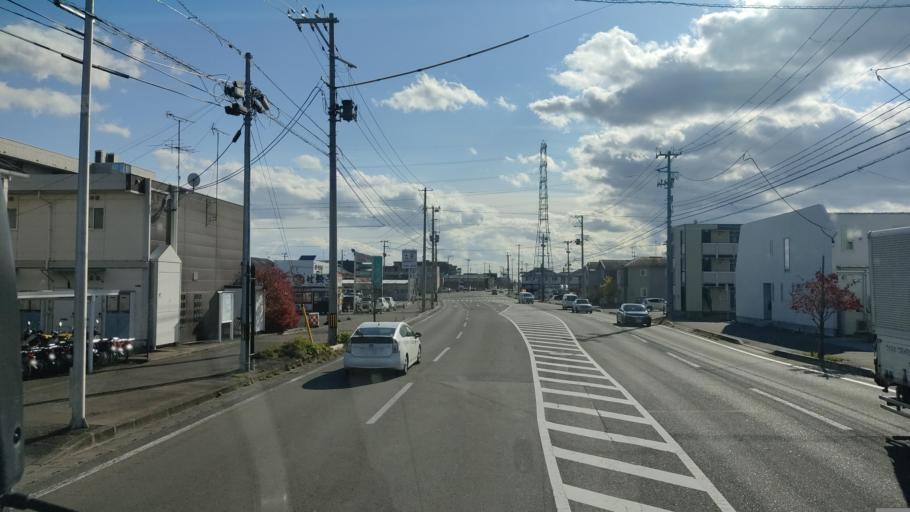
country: JP
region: Iwate
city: Morioka-shi
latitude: 39.6811
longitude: 141.1432
